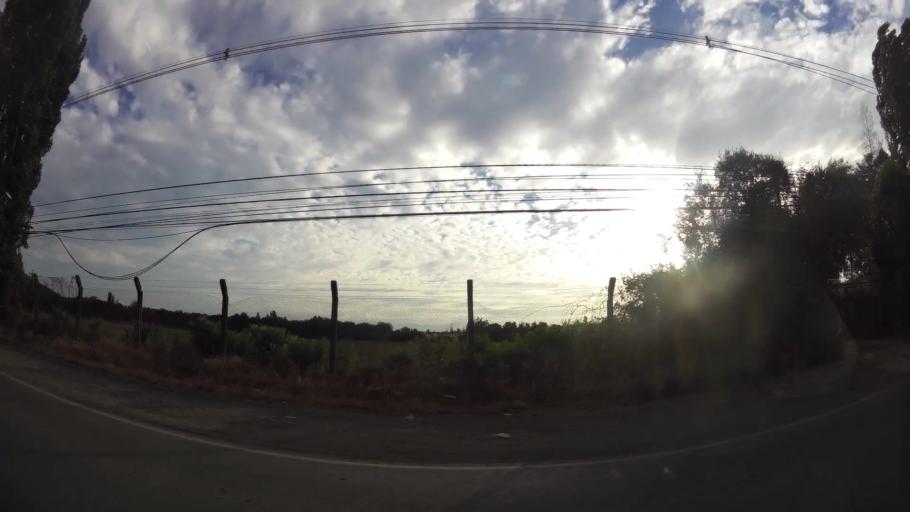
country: CL
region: Santiago Metropolitan
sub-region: Provincia de Maipo
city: San Bernardo
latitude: -33.6416
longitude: -70.6703
